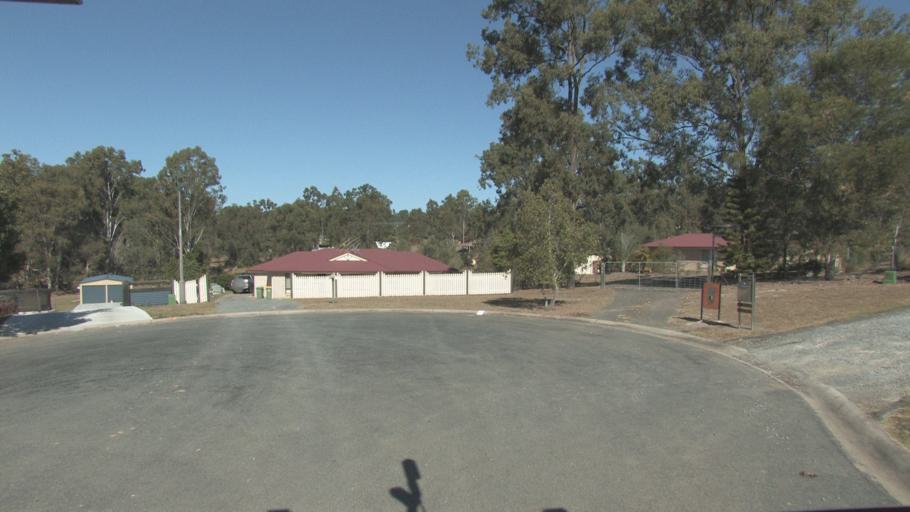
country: AU
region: Queensland
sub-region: Logan
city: Cedar Vale
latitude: -27.8647
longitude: 153.0391
